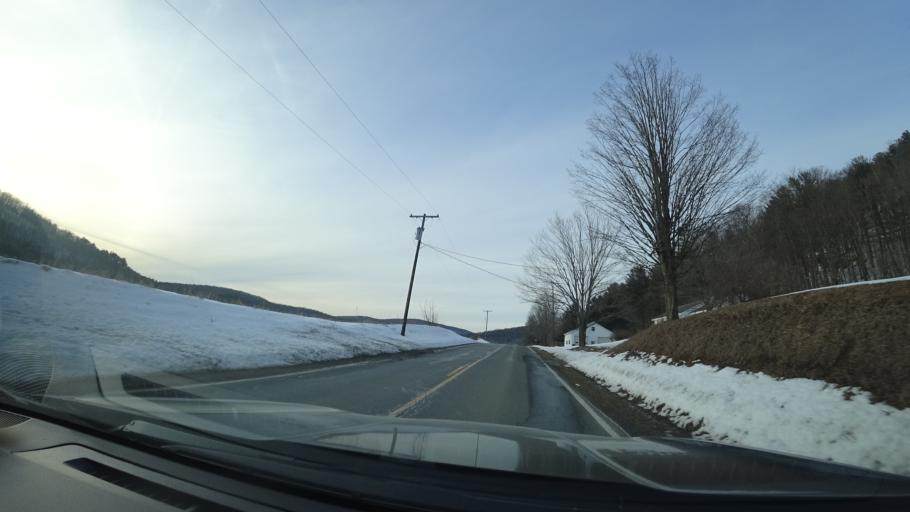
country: US
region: New York
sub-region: Washington County
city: Cambridge
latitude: 43.1820
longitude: -73.3672
